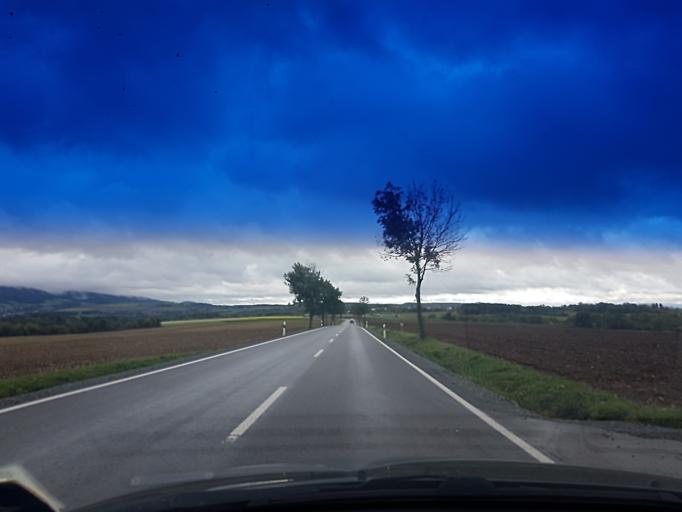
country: DE
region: Bavaria
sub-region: Upper Franconia
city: Bindlach
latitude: 50.0107
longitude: 11.6146
